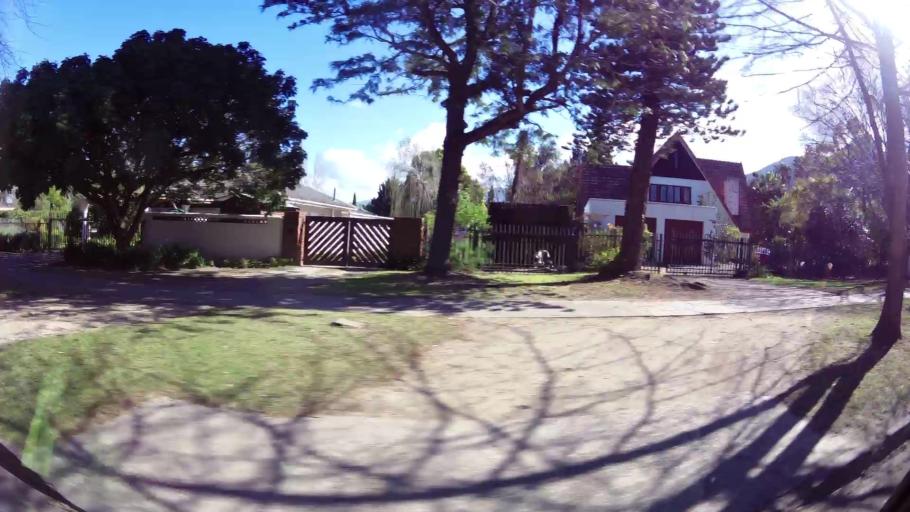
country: ZA
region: Western Cape
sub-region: Eden District Municipality
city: George
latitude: -33.9490
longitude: 22.4629
